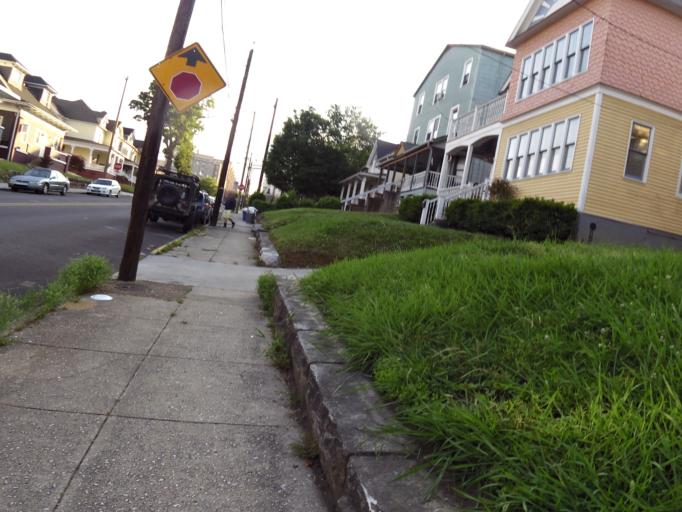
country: US
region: Tennessee
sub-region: Knox County
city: Knoxville
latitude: 35.9608
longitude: -83.9270
